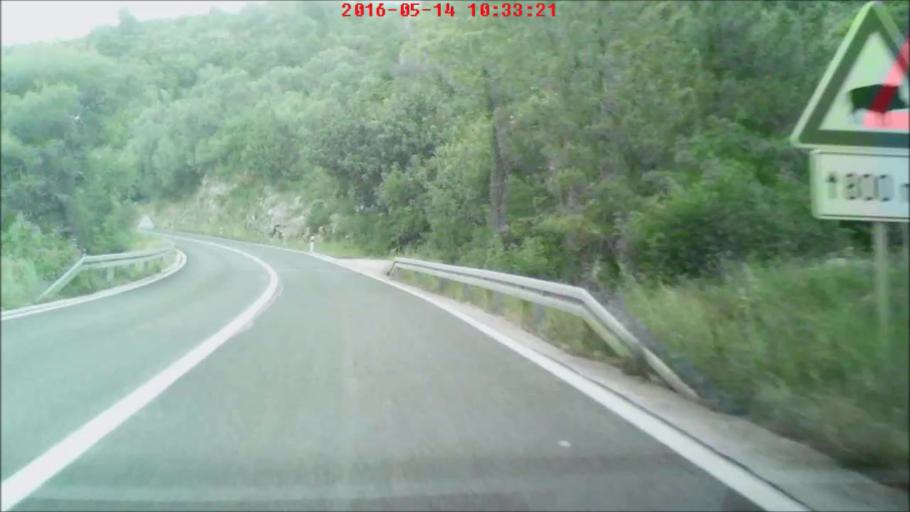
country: HR
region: Dubrovacko-Neretvanska
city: Podgora
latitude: 42.7727
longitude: 17.8865
